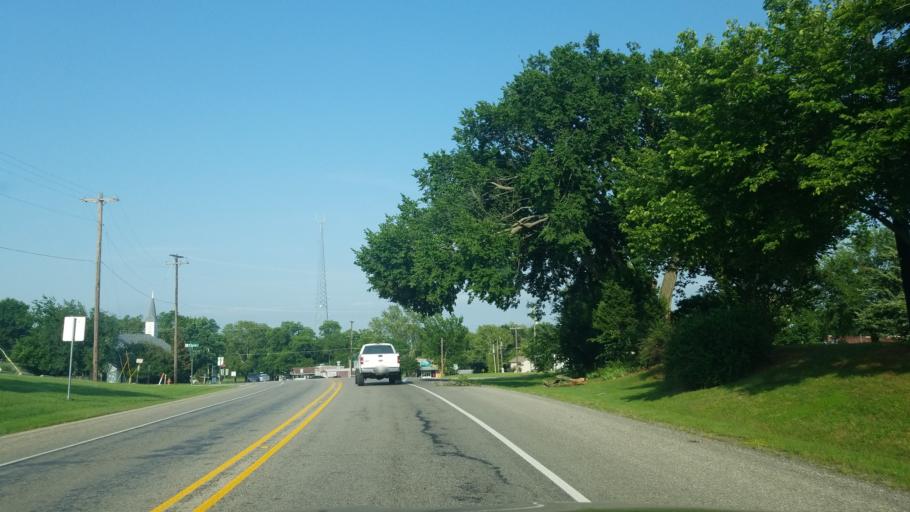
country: US
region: Texas
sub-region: Denton County
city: Aubrey
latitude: 33.3043
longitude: -96.9880
